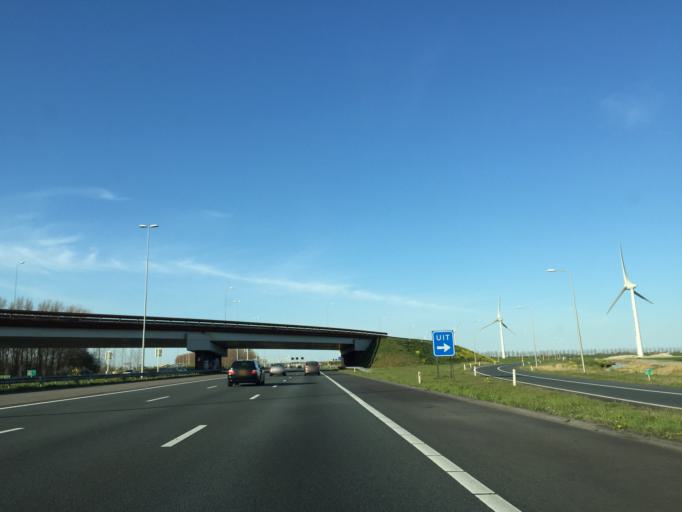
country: NL
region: South Holland
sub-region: Gemeente Kaag en Braassem
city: Oude Wetering
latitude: 52.2316
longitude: 4.6465
